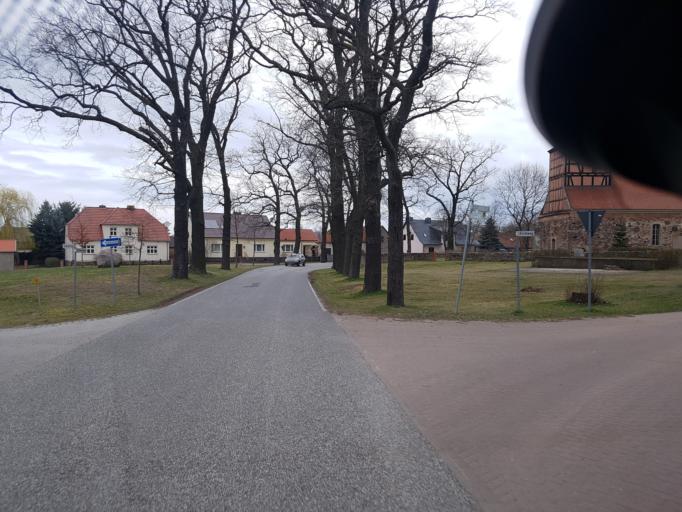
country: DE
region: Brandenburg
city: Mixdorf
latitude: 52.1975
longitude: 14.3430
